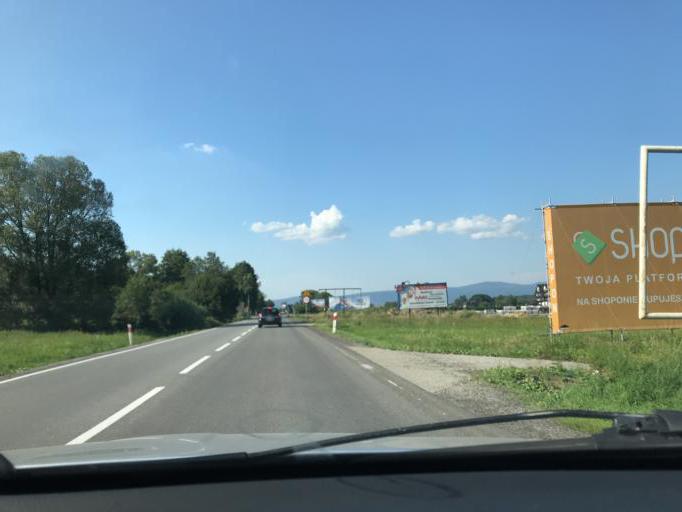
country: PL
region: Lesser Poland Voivodeship
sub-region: Powiat tatrzanski
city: Bialy Dunajec
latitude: 49.3957
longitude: 20.0169
